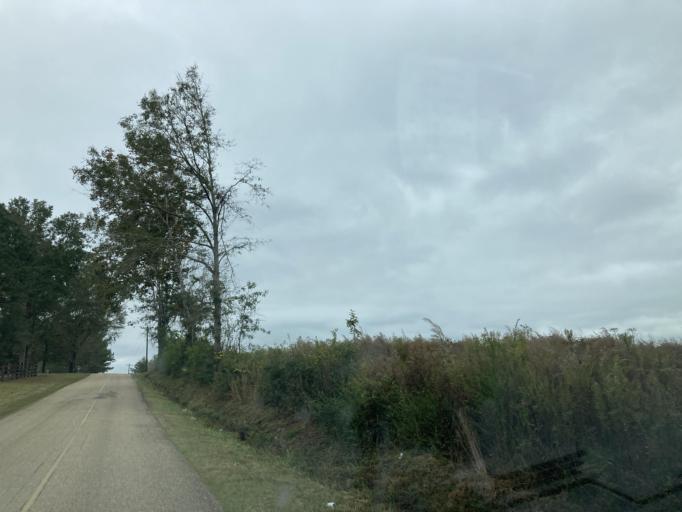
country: US
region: Mississippi
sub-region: Lamar County
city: West Hattiesburg
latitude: 31.2651
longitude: -89.5058
